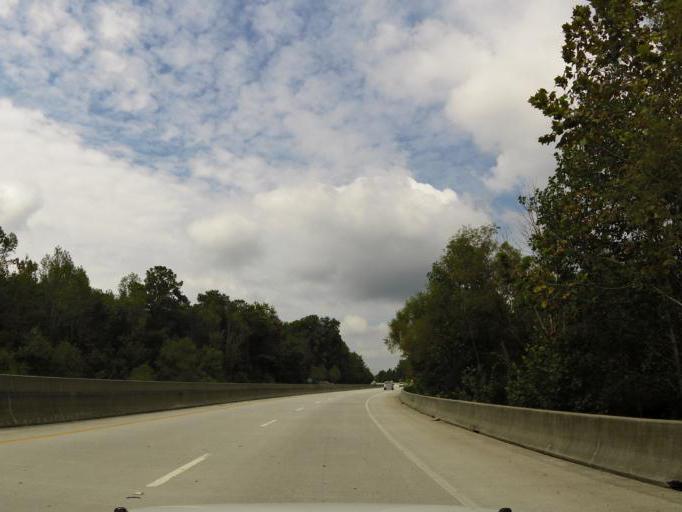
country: US
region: Georgia
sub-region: Cobb County
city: Powder Springs
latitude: 33.9168
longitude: -84.6288
